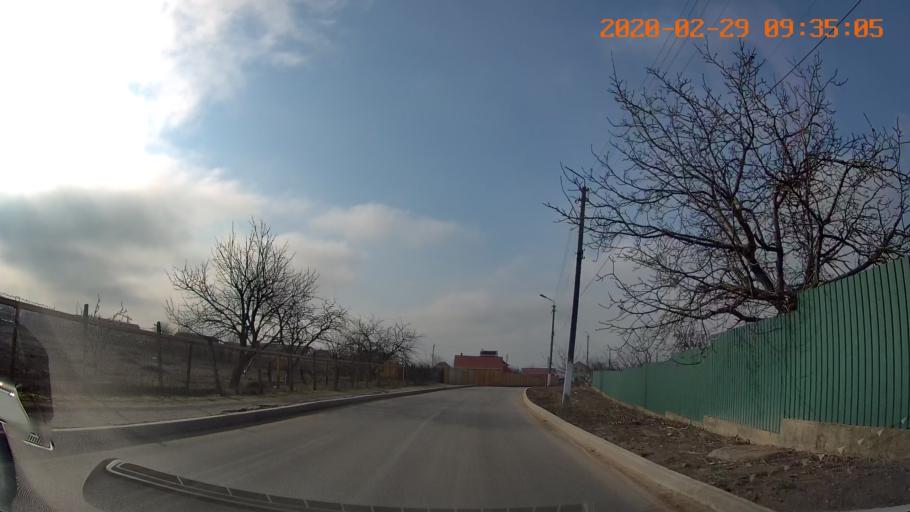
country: MD
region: Telenesti
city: Dnestrovsc
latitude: 46.6195
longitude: 29.9020
